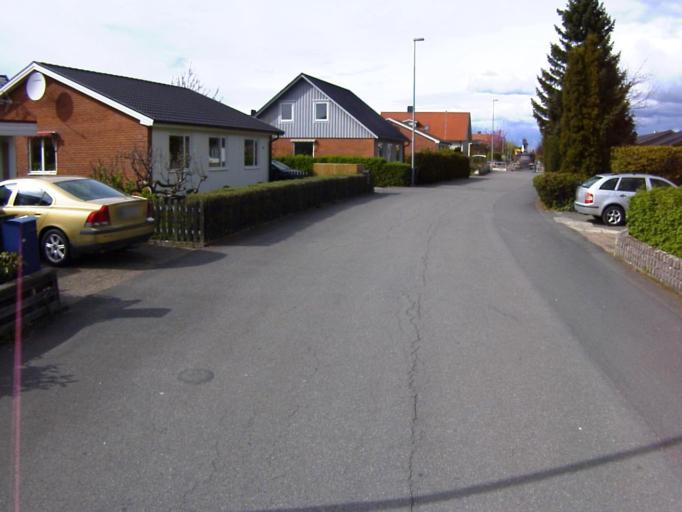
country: SE
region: Skane
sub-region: Kristianstads Kommun
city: Kristianstad
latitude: 56.0461
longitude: 14.1702
